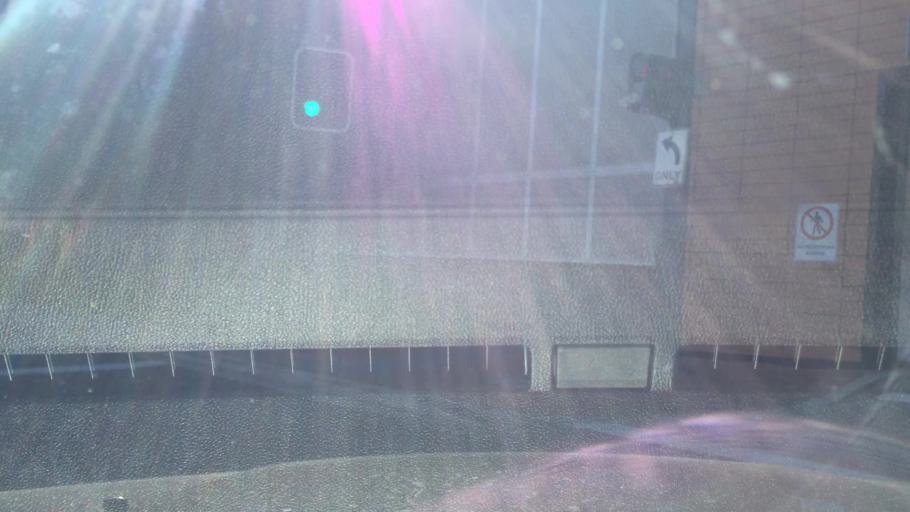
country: AU
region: New South Wales
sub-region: Fairfield
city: Liverpool
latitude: -33.9185
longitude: 150.9221
